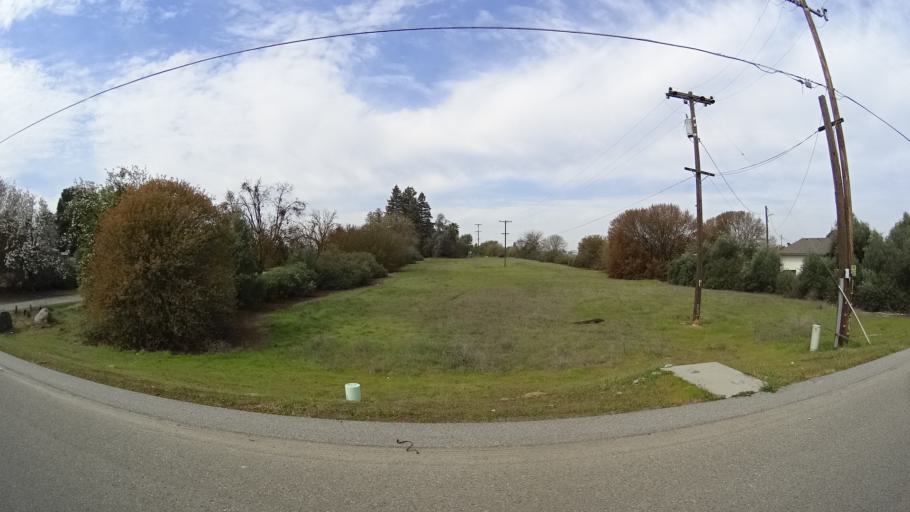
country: US
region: California
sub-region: Fresno County
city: West Park
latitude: 36.7837
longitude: -119.8984
